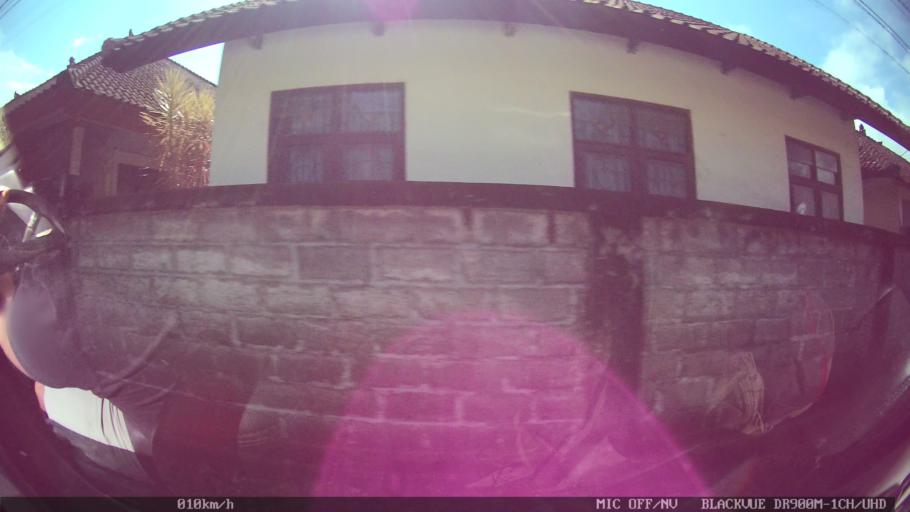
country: ID
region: Bali
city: Banjar Sedang
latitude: -8.5568
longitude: 115.2692
